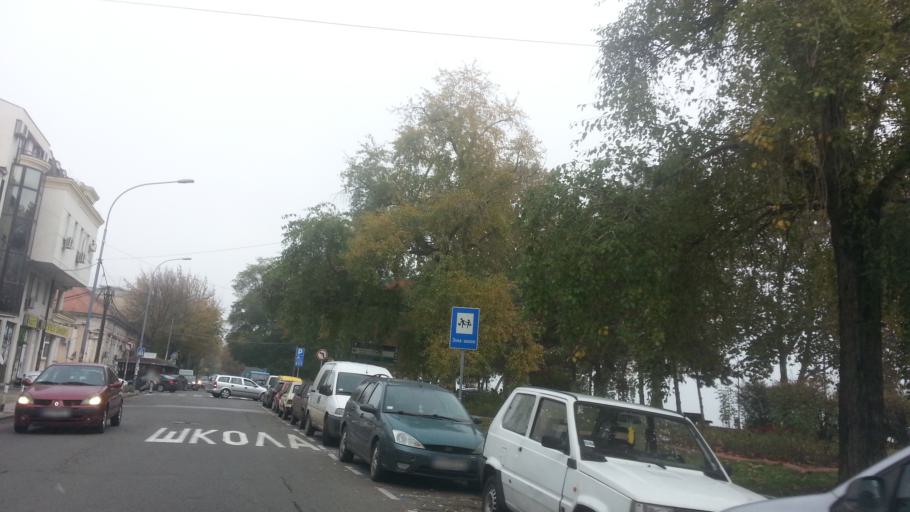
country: RS
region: Central Serbia
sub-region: Belgrade
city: Zemun
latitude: 44.8443
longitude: 20.4163
